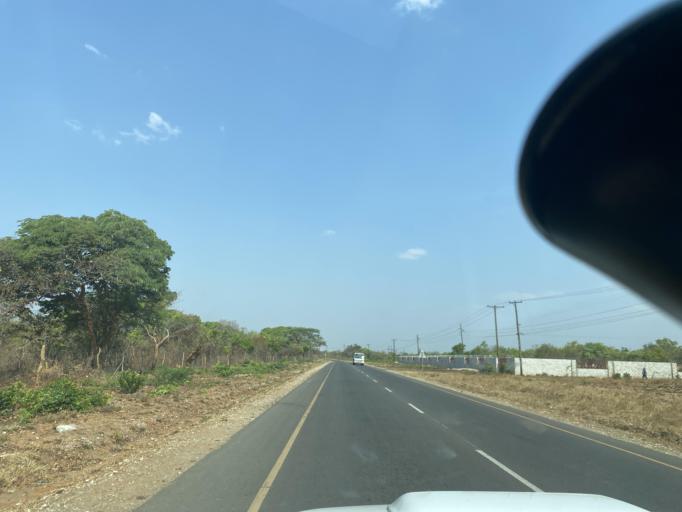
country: ZM
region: Lusaka
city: Lusaka
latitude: -15.3475
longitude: 28.0973
